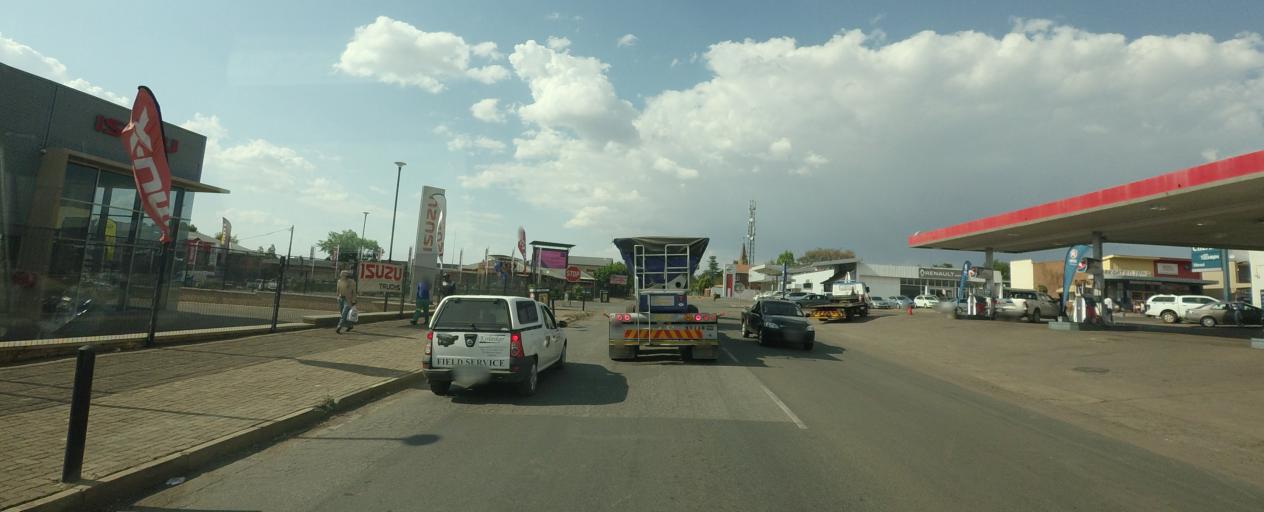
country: ZA
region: Mpumalanga
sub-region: Ehlanzeni District
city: Lydenburg
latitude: -25.0962
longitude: 30.4553
